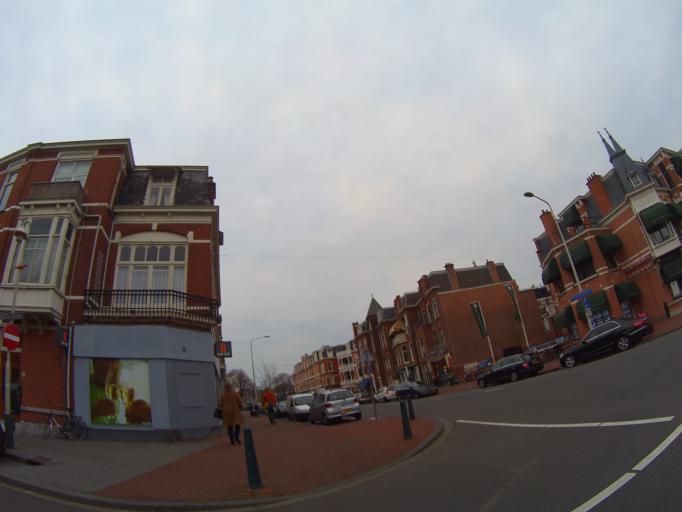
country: NL
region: South Holland
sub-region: Gemeente Den Haag
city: Scheveningen
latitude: 52.0876
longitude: 4.2777
